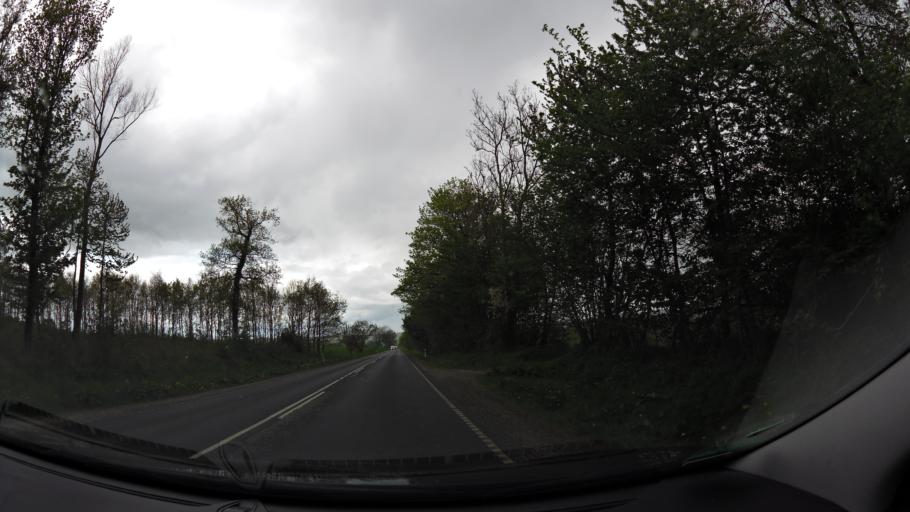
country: DK
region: South Denmark
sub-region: Nyborg Kommune
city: Nyborg
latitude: 55.2739
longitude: 10.7664
